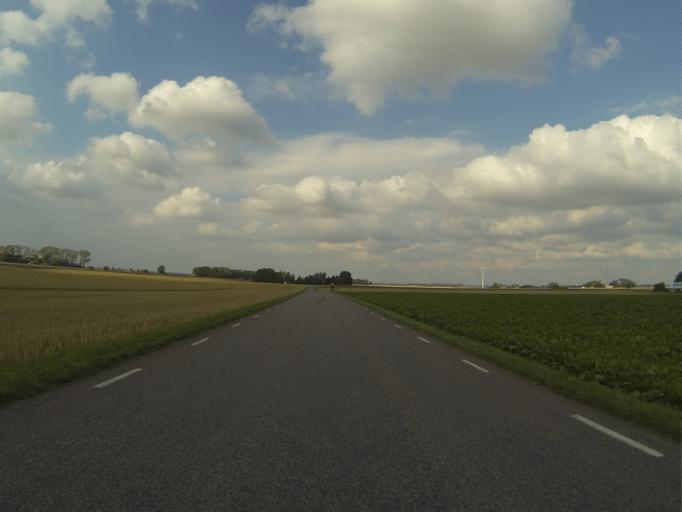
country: SE
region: Skane
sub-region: Lunds Kommun
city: Lund
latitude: 55.7699
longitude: 13.1777
